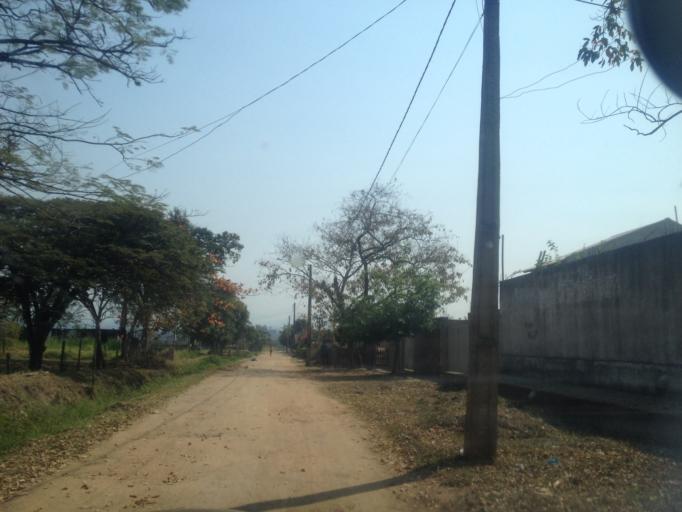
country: BR
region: Rio de Janeiro
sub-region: Porto Real
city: Porto Real
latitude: -22.4332
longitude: -44.3401
